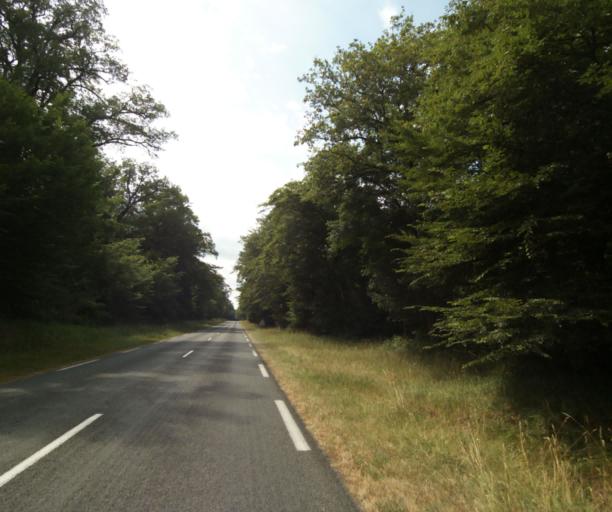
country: FR
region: Ile-de-France
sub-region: Departement de Seine-et-Marne
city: Fontainebleau
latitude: 48.4101
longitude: 2.6762
